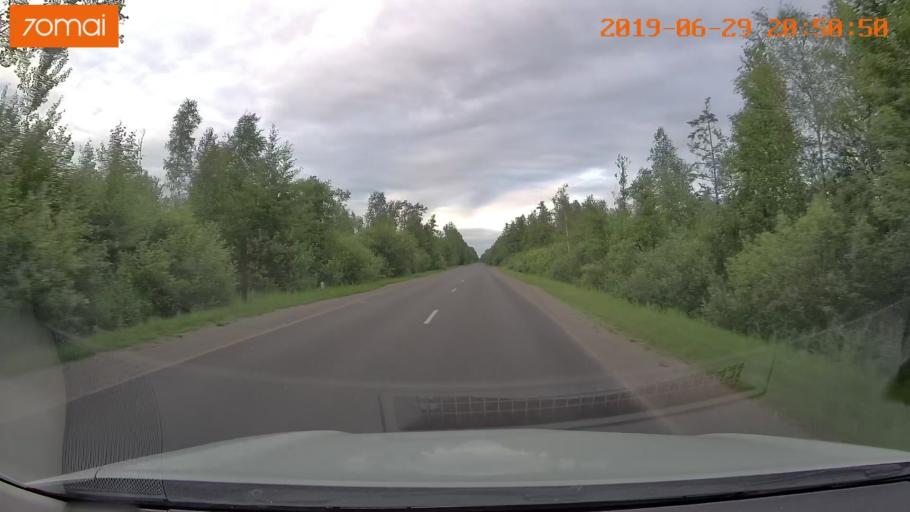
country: BY
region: Brest
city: Hantsavichy
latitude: 52.6810
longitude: 26.3412
